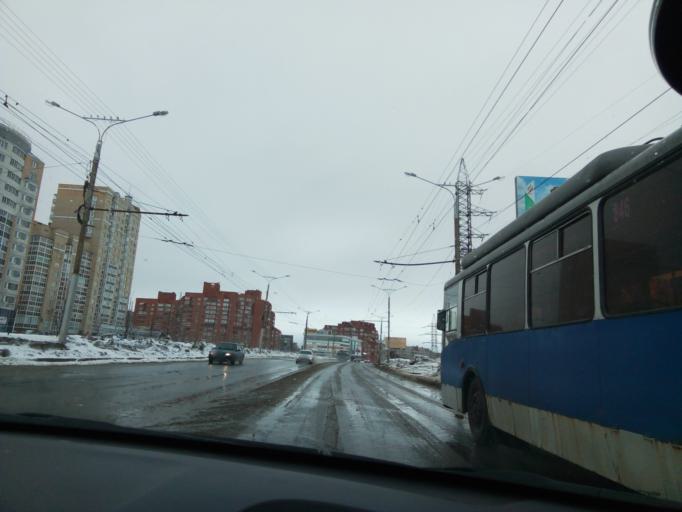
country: RU
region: Chuvashia
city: Novyye Lapsary
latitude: 56.1342
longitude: 47.1648
